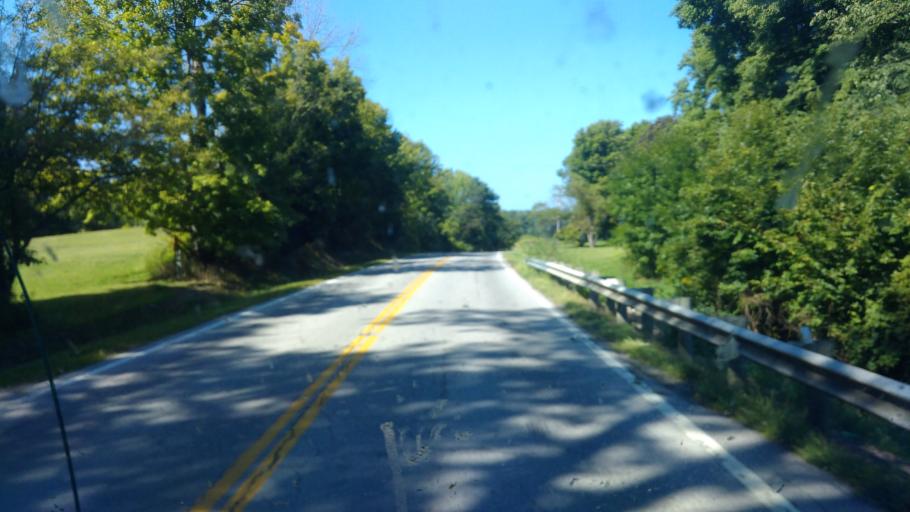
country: US
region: Ohio
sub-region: Ashland County
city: Ashland
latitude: 40.9440
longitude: -82.2660
